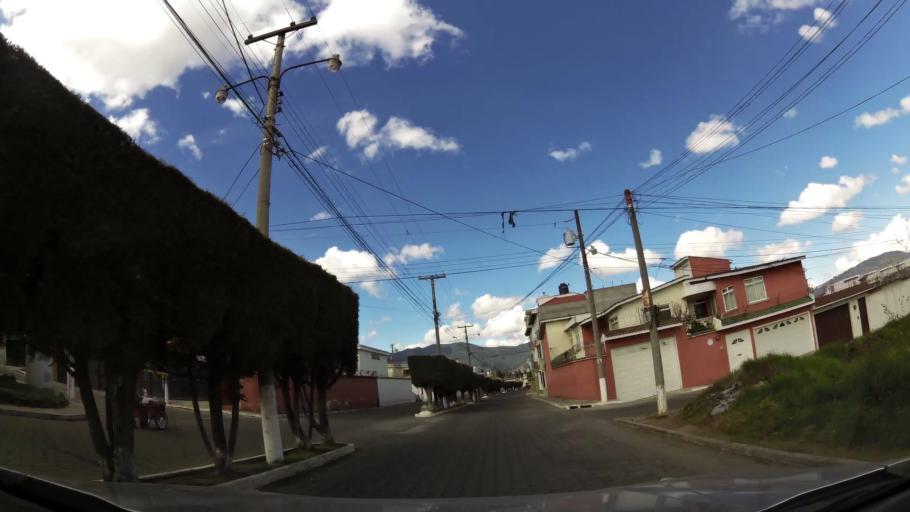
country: GT
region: Quetzaltenango
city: Quetzaltenango
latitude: 14.8473
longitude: -91.5411
